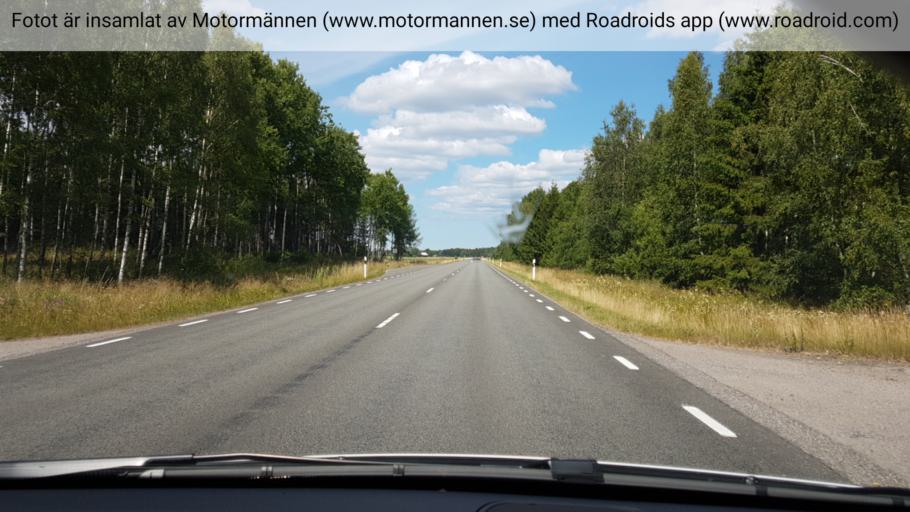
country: SE
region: Vaestra Goetaland
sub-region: Mariestads Kommun
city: Mariestad
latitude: 58.6361
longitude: 13.9173
